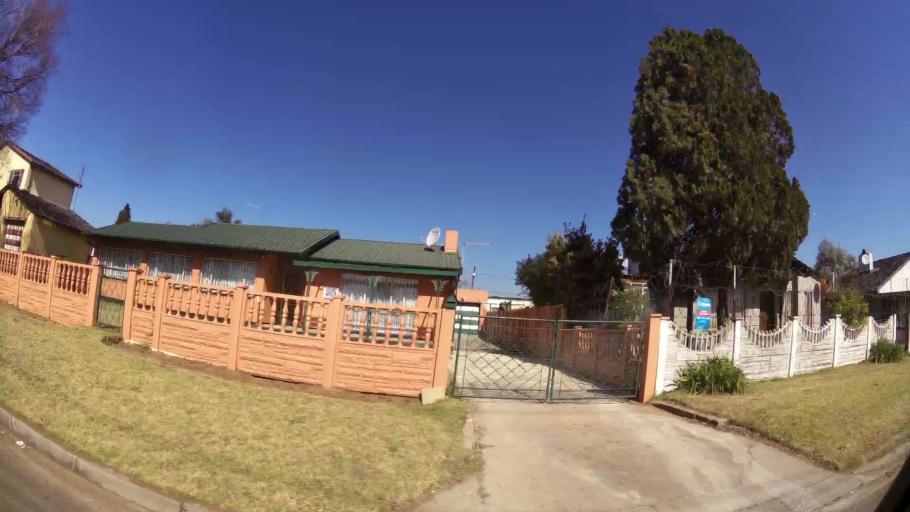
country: ZA
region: Gauteng
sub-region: City of Johannesburg Metropolitan Municipality
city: Johannesburg
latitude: -26.2367
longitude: 28.0664
